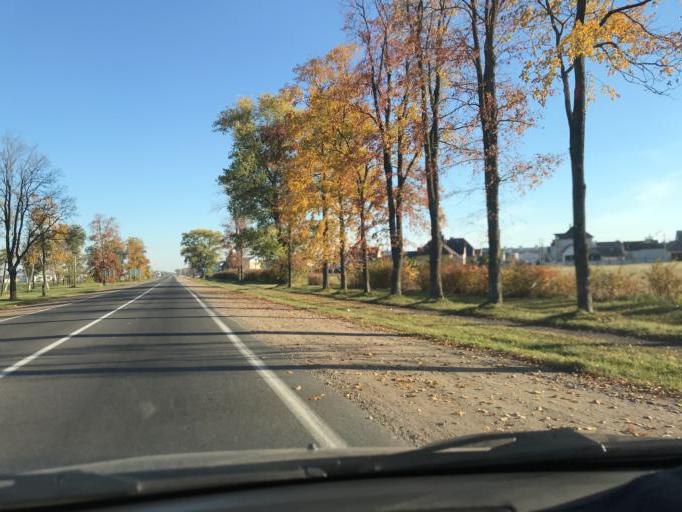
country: BY
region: Minsk
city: Slutsk
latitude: 53.0520
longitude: 27.5556
